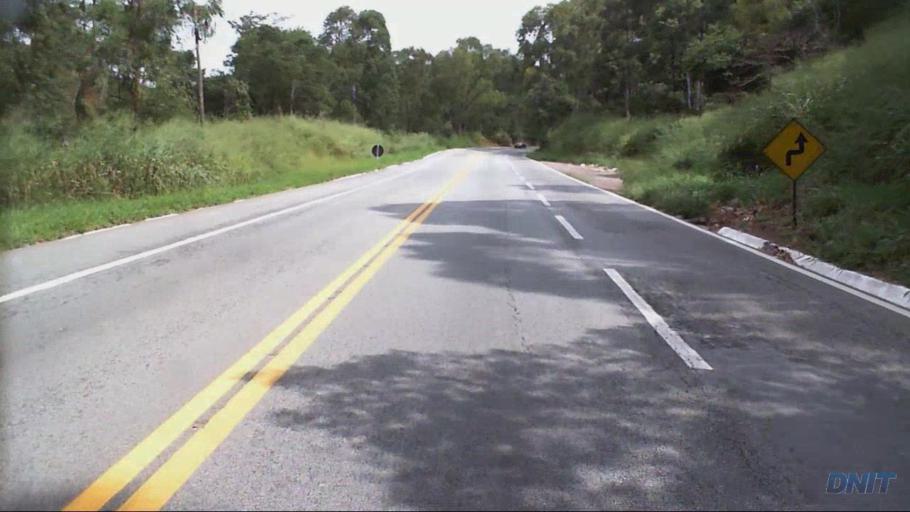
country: BR
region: Minas Gerais
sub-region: Caete
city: Caete
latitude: -19.7361
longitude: -43.5998
